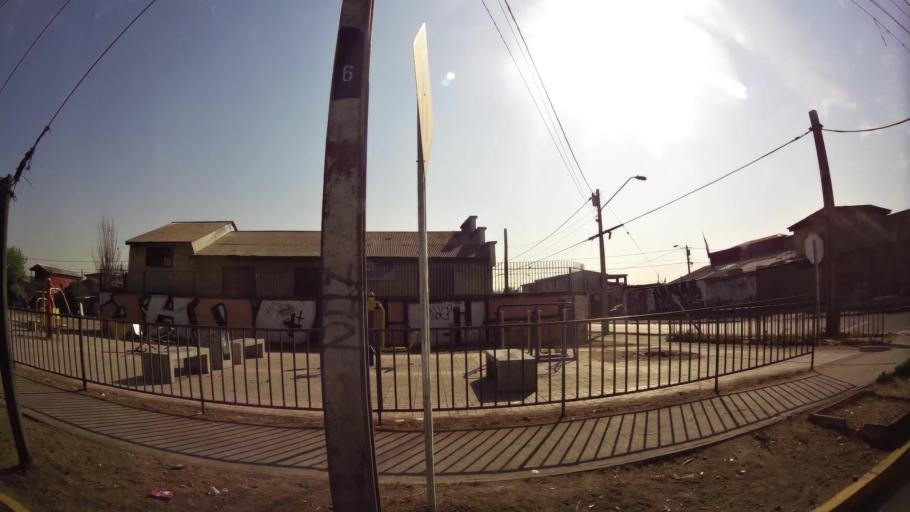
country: CL
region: Santiago Metropolitan
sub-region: Provincia de Maipo
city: San Bernardo
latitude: -33.5213
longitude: -70.7000
